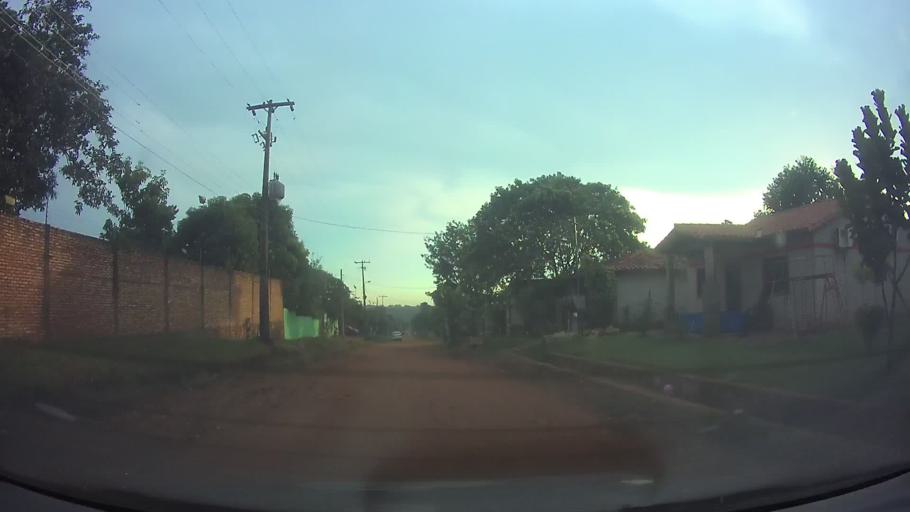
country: PY
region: Central
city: Limpio
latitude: -25.2451
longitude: -57.4553
